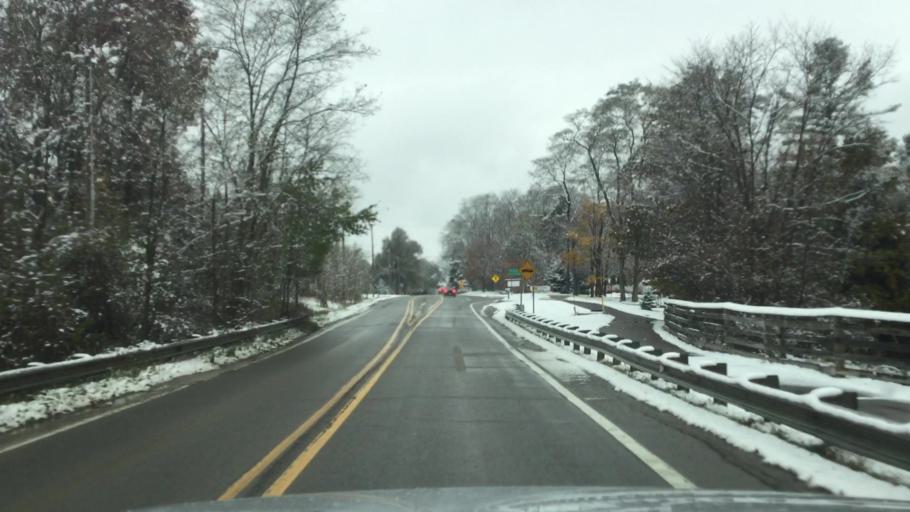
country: US
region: Michigan
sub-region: Oakland County
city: Oxford
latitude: 42.8095
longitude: -83.2844
